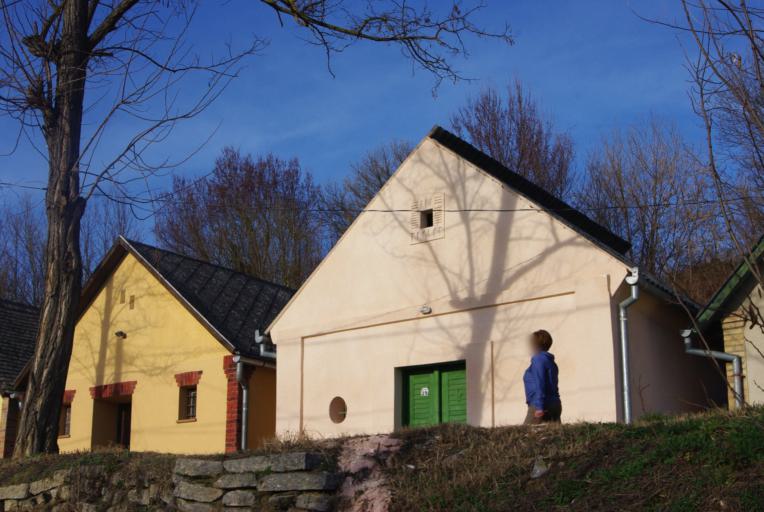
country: HU
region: Tolna
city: Bolcske
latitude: 46.7429
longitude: 18.9613
